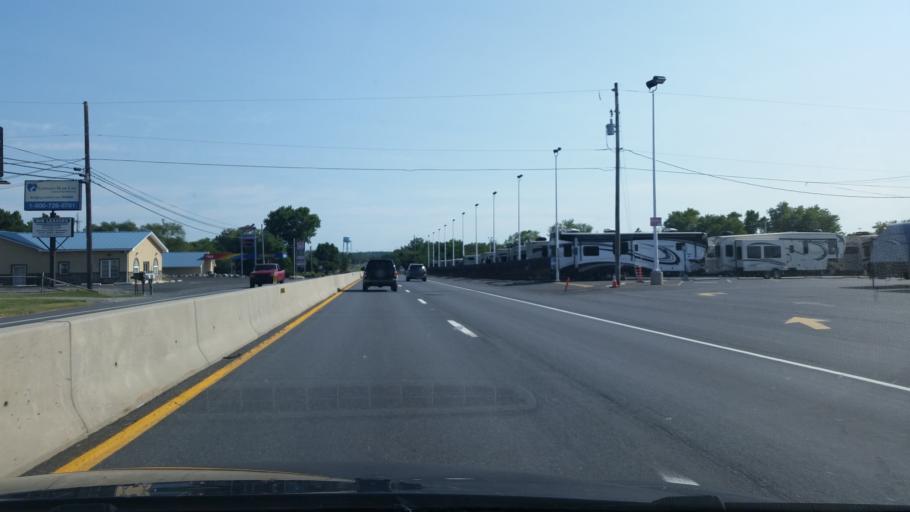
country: US
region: Pennsylvania
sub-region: Berks County
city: Shoemakersville
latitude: 40.5152
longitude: -75.9678
